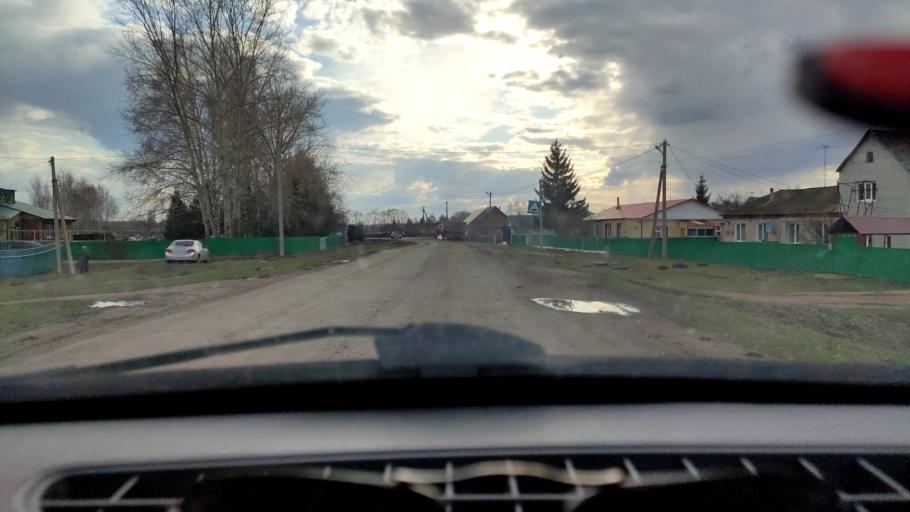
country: RU
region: Bashkortostan
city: Karmaskaly
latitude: 54.3773
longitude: 56.2070
